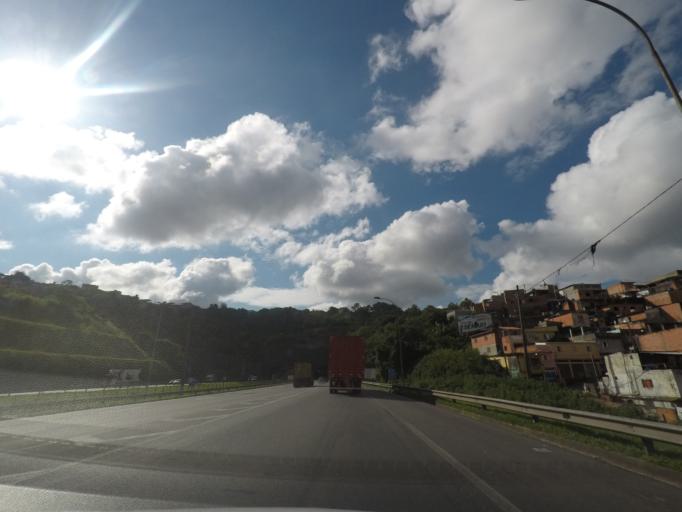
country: BR
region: Sao Paulo
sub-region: Embu
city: Embu
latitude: -23.6278
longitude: -46.8293
